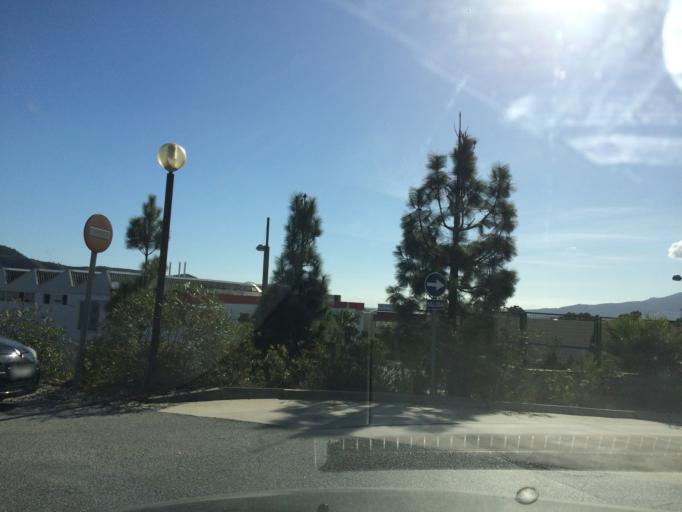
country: ES
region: Andalusia
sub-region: Provincia de Malaga
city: Estacion de Cartama
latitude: 36.7343
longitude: -4.5477
